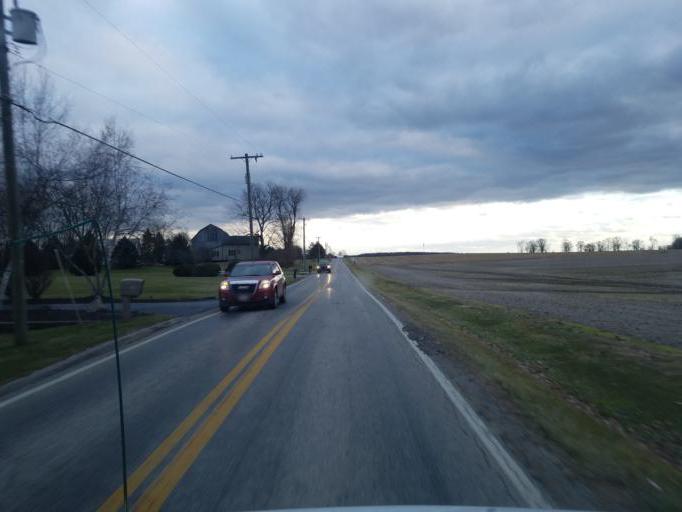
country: US
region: Ohio
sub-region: Delaware County
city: Delaware
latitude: 40.3354
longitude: -83.1182
